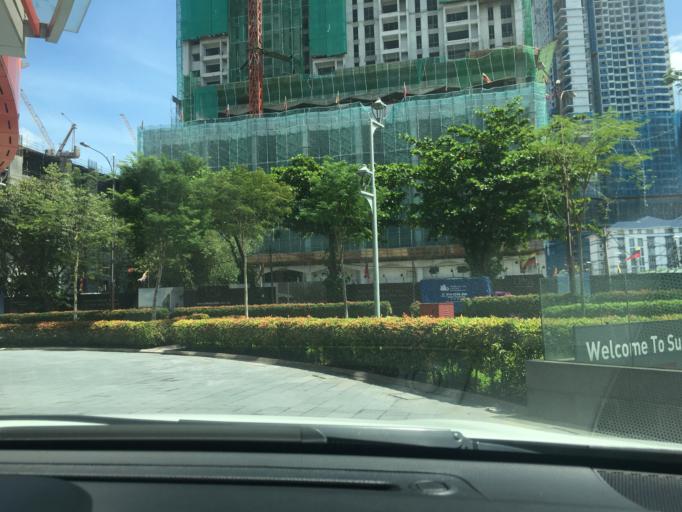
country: MY
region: Kuala Lumpur
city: Kuala Lumpur
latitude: 3.1267
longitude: 101.7255
